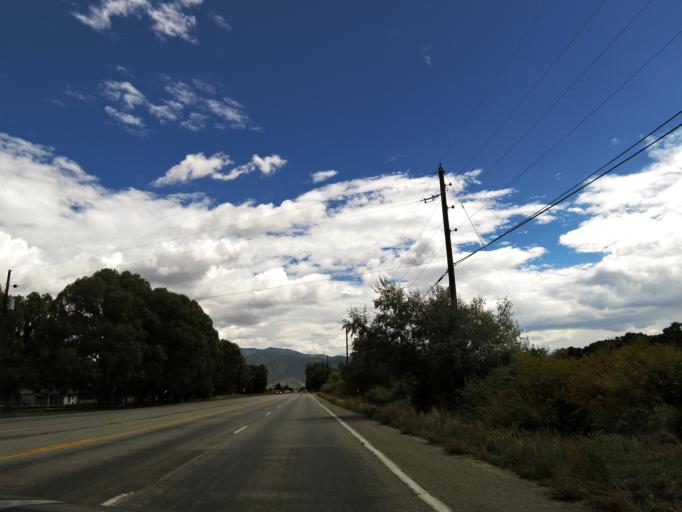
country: US
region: Colorado
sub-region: Chaffee County
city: Salida
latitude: 38.5198
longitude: -106.0419
